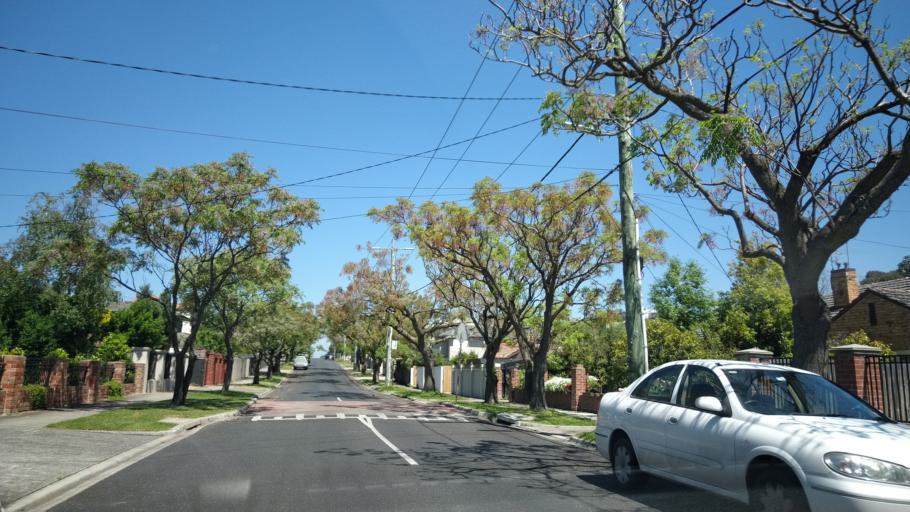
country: AU
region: Victoria
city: Ormond
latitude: -37.9002
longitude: 145.0308
